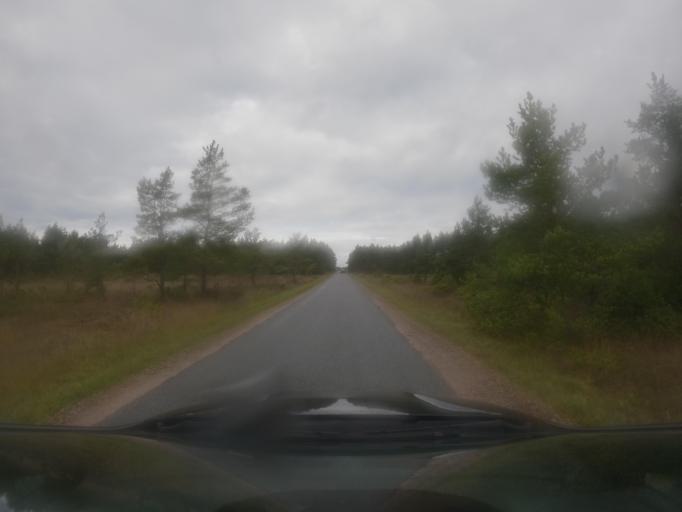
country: EE
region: Saare
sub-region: Kuressaare linn
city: Kuressaare
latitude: 58.4411
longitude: 21.9882
